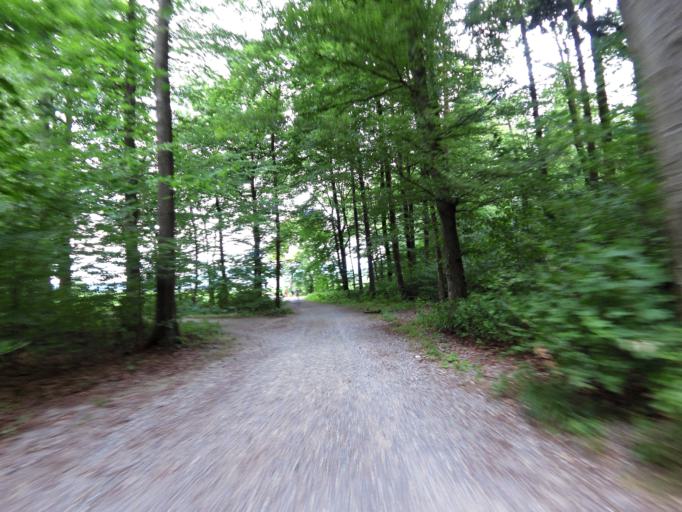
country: CH
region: Zurich
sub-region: Bezirk Zuerich
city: Zuerich (Kreis 5) / Escher-Wyss
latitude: 47.4043
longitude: 8.5145
